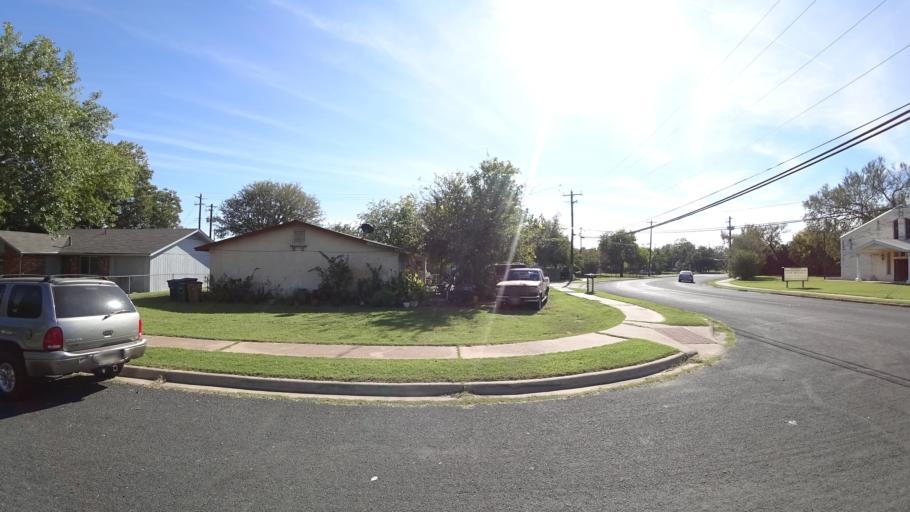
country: US
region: Texas
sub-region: Travis County
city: Austin
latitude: 30.2564
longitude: -97.6838
